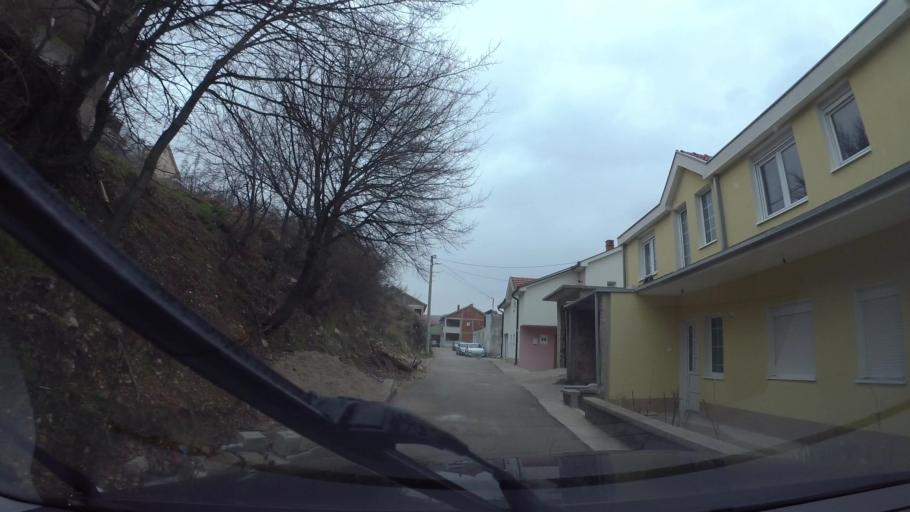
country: BA
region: Federation of Bosnia and Herzegovina
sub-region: Hercegovacko-Bosanski Kanton
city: Mostar
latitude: 43.3587
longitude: 17.8178
